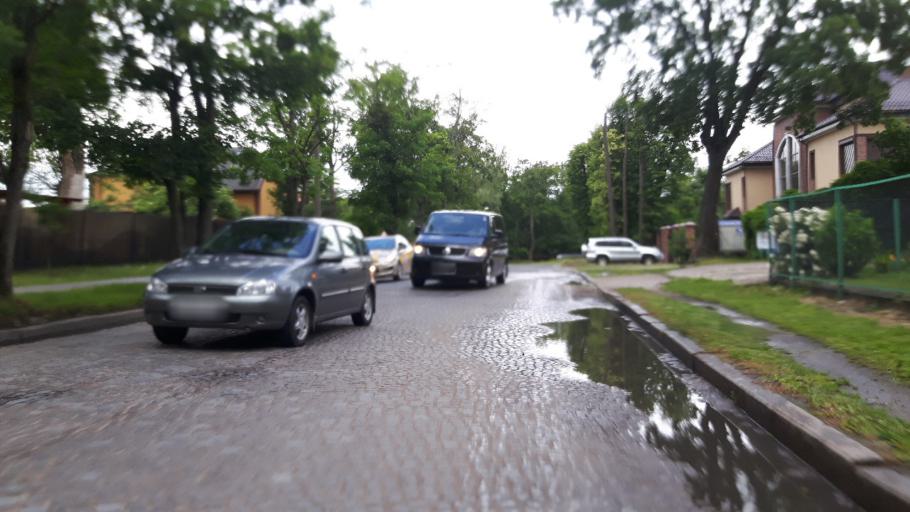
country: RU
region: Kaliningrad
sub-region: Gorod Kaliningrad
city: Kaliningrad
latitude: 54.7343
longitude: 20.5177
